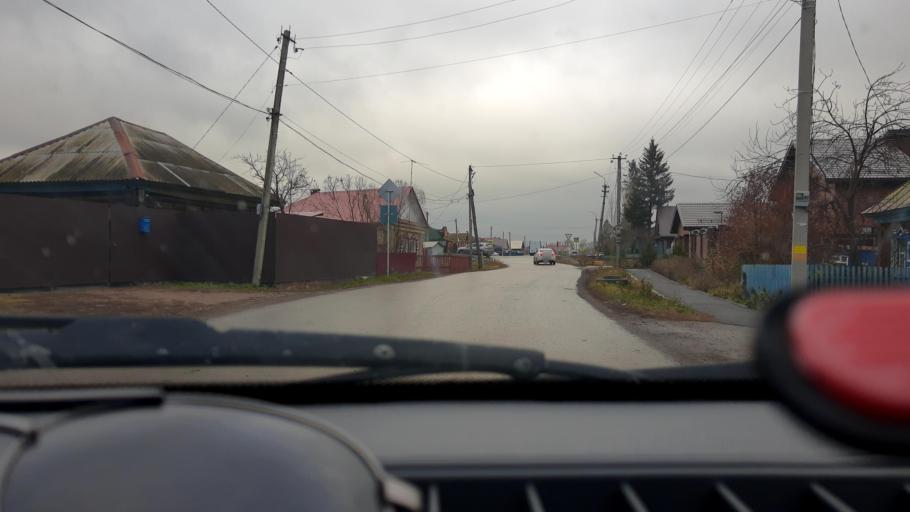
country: RU
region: Bashkortostan
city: Ufa
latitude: 54.6106
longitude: 55.9005
